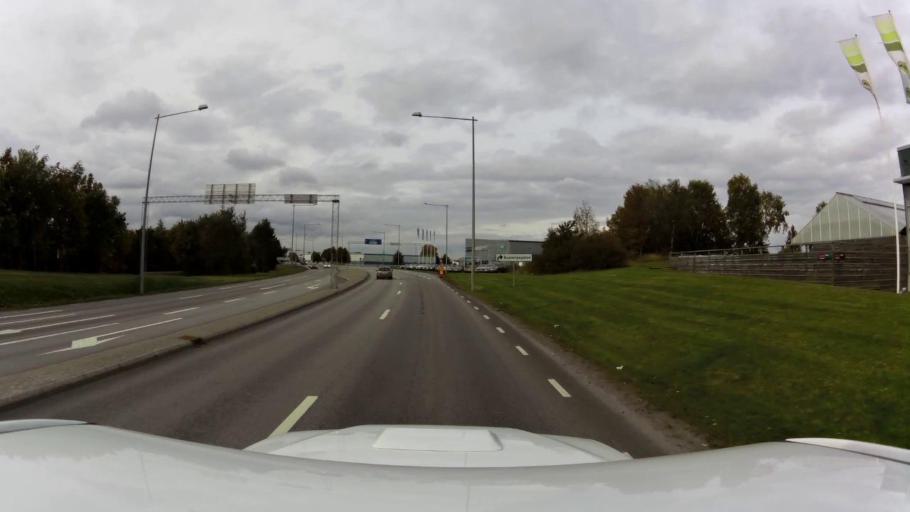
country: SE
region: OEstergoetland
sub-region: Linkopings Kommun
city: Linkoping
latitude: 58.4298
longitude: 15.6024
